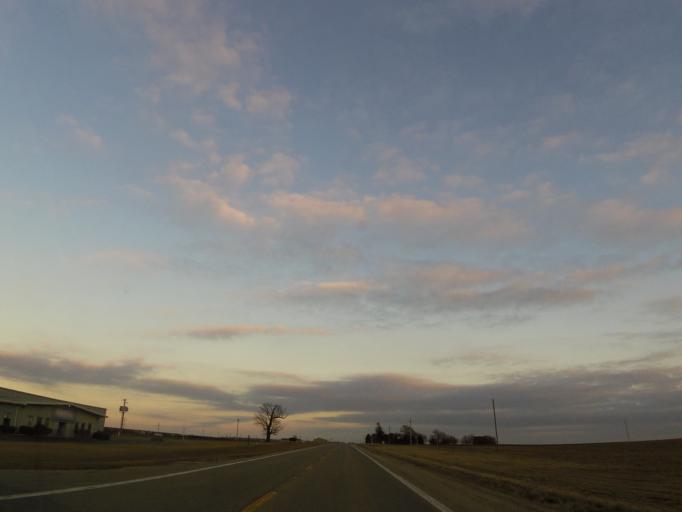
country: US
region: Illinois
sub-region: McLean County
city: Gridley
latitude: 40.7390
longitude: -88.9315
